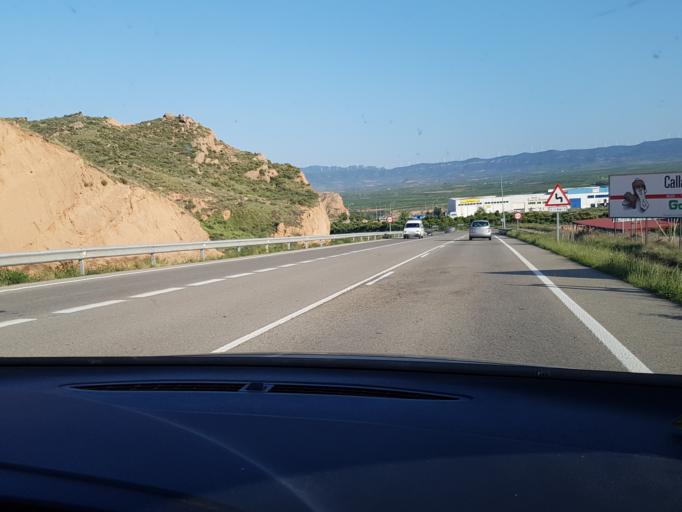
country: ES
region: La Rioja
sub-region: Provincia de La Rioja
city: Arnedo
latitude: 42.2379
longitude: -2.0858
